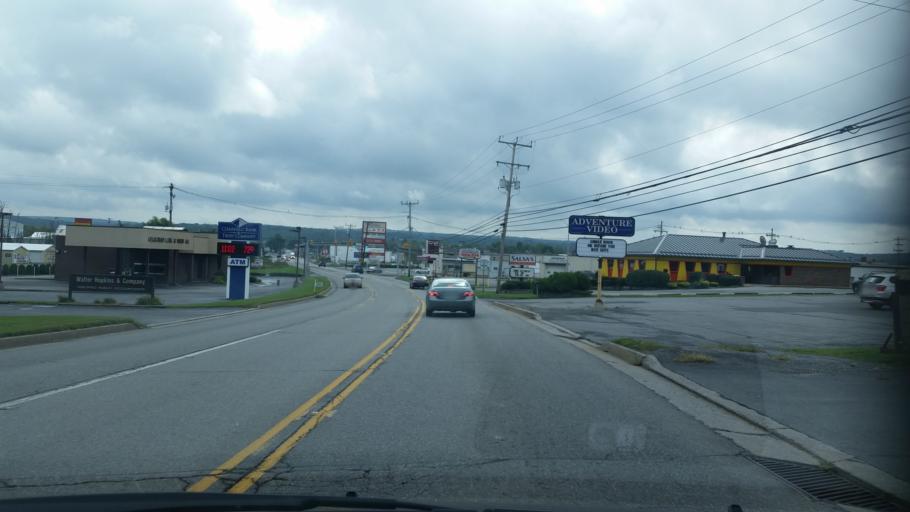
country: US
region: Pennsylvania
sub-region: Centre County
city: Philipsburg
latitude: 40.9050
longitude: -78.2347
